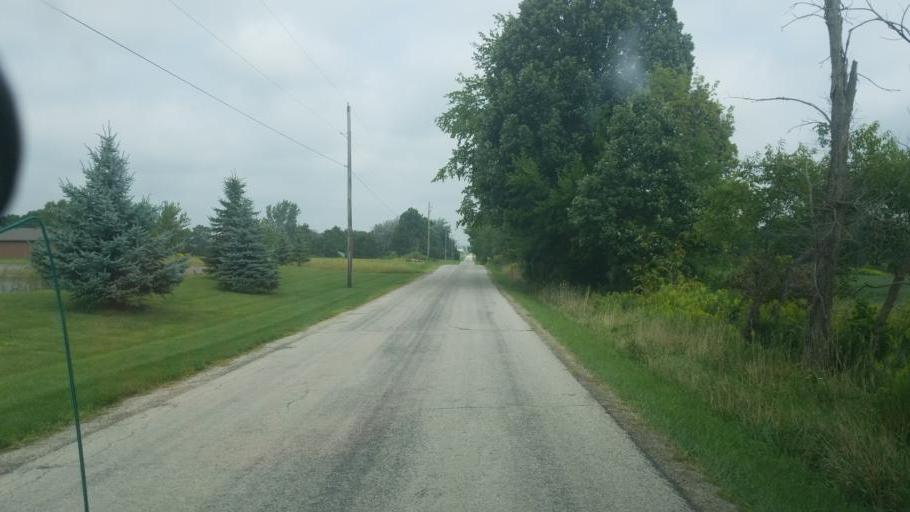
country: US
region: Ohio
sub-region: Richland County
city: Shelby
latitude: 40.8681
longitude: -82.5520
